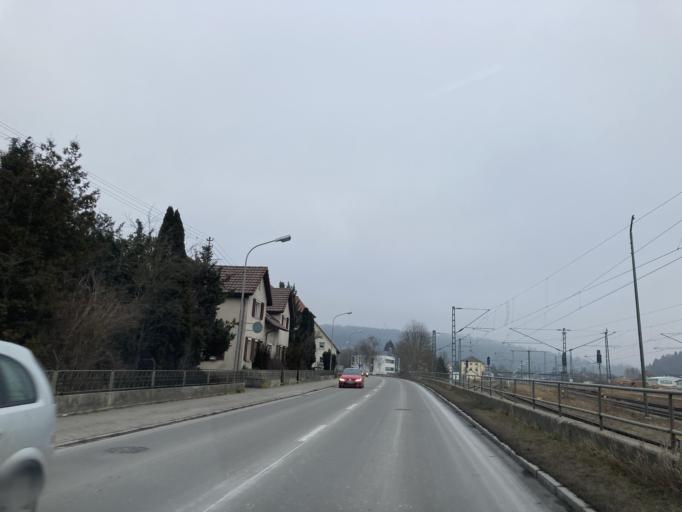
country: DE
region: Baden-Wuerttemberg
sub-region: Freiburg Region
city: Immendingen
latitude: 47.9355
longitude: 8.7242
